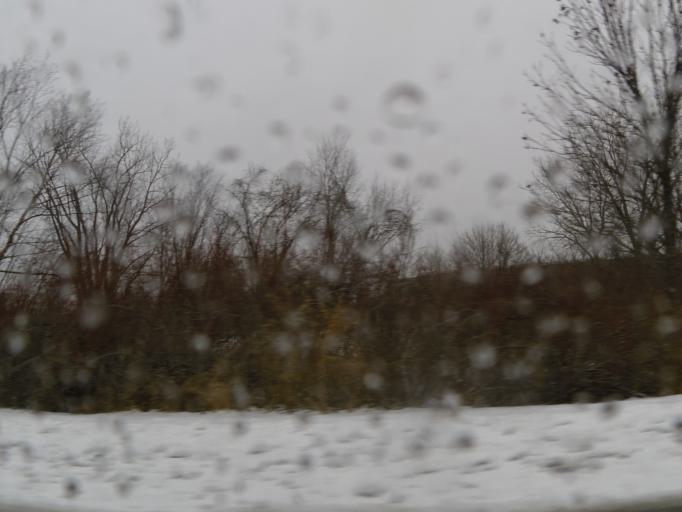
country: US
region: Minnesota
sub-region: Washington County
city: Oakdale
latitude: 44.9550
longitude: -92.9318
